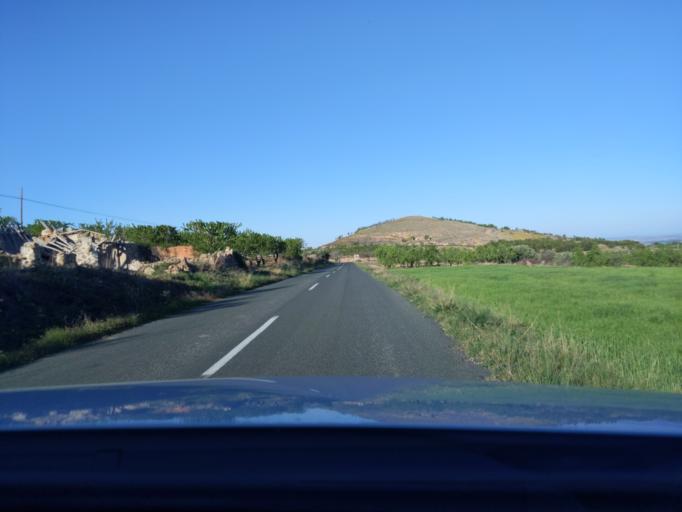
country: ES
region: La Rioja
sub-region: Provincia de La Rioja
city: Bergasa
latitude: 42.2683
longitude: -2.1004
